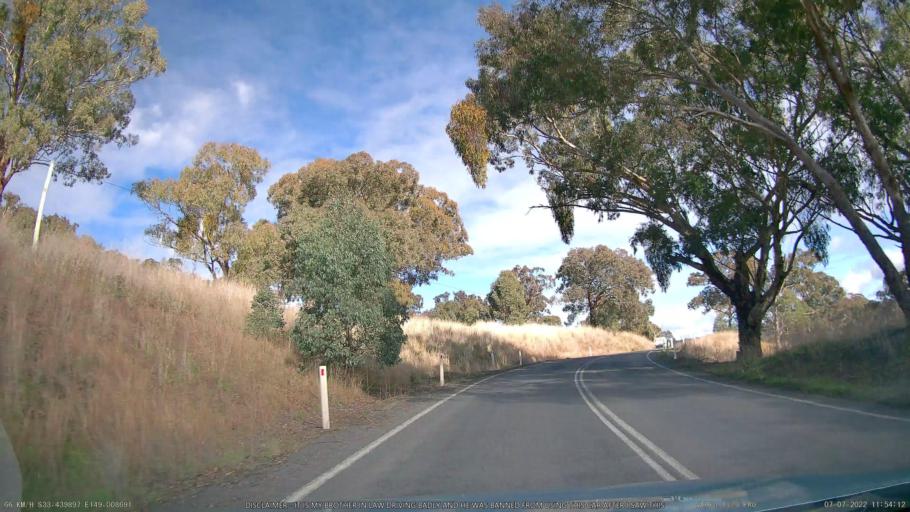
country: AU
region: New South Wales
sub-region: Blayney
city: Millthorpe
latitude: -33.4402
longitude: 149.0083
